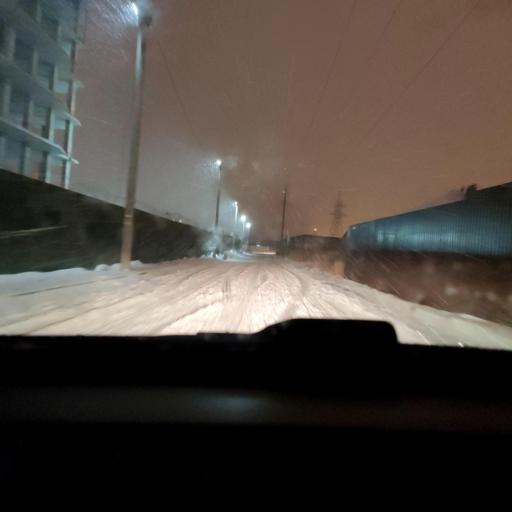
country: RU
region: Voronezj
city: Podgornoye
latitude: 51.7193
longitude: 39.1475
